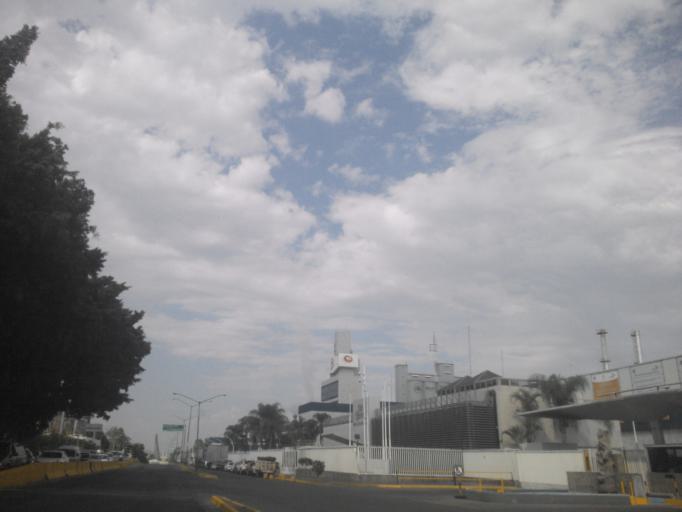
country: MX
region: Jalisco
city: Guadalajara
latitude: 20.6631
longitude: -103.3771
